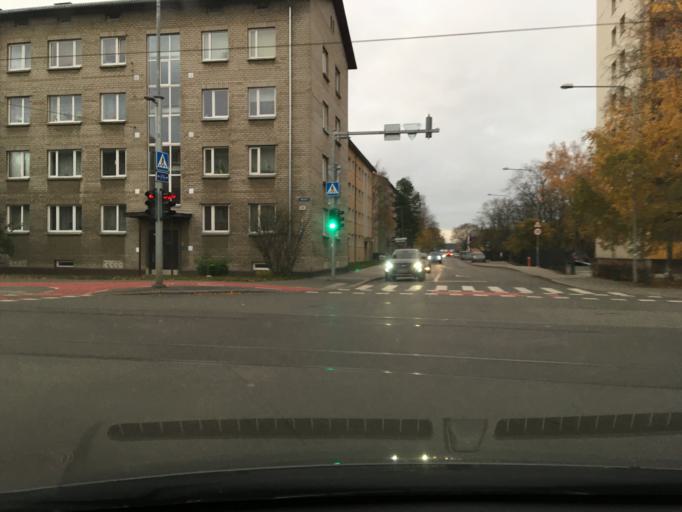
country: EE
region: Harju
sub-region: Tallinna linn
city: Tallinn
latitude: 59.4288
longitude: 24.7902
